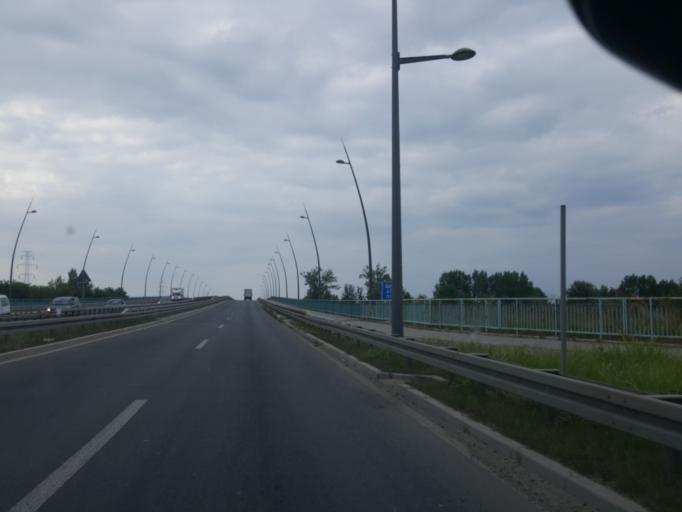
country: RS
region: Autonomna Pokrajina Vojvodina
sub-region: Juznobacki Okrug
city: Novi Sad
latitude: 45.2825
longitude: 19.8037
